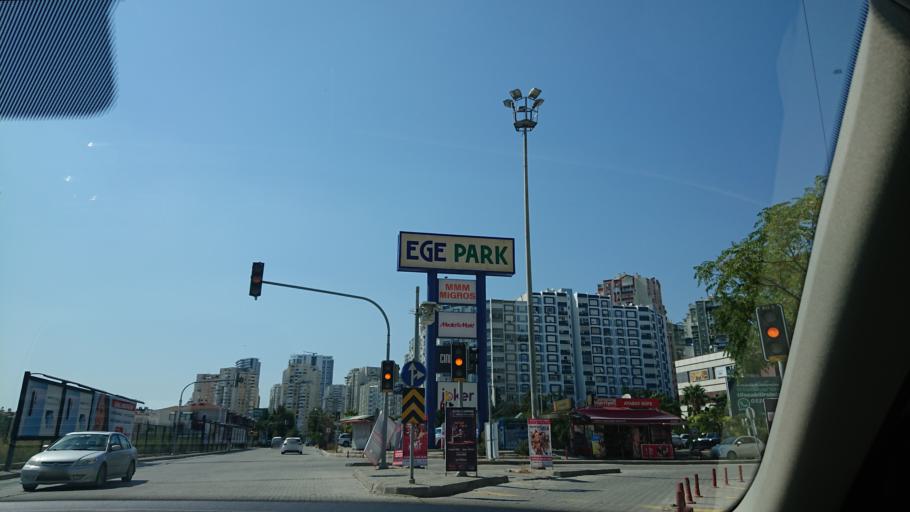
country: TR
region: Izmir
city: Karsiyaka
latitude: 38.4696
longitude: 27.0759
